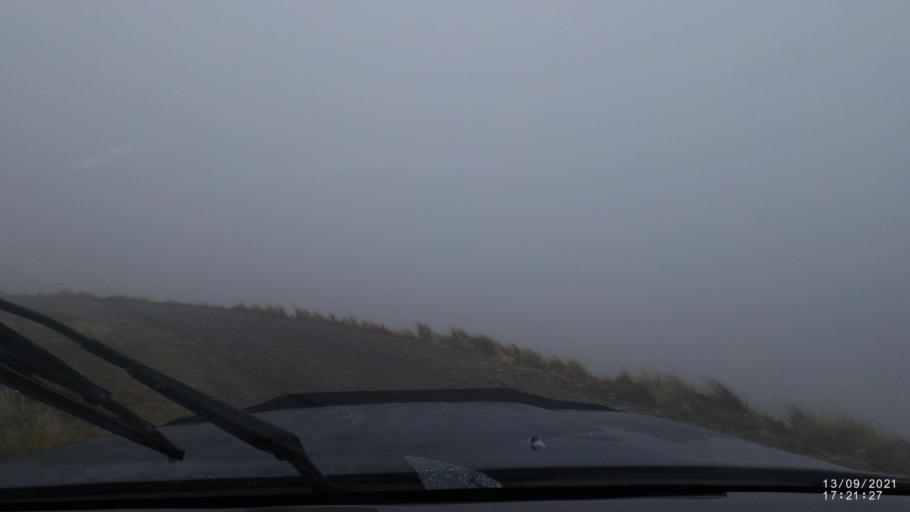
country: BO
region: Cochabamba
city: Colomi
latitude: -17.3499
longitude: -65.7668
